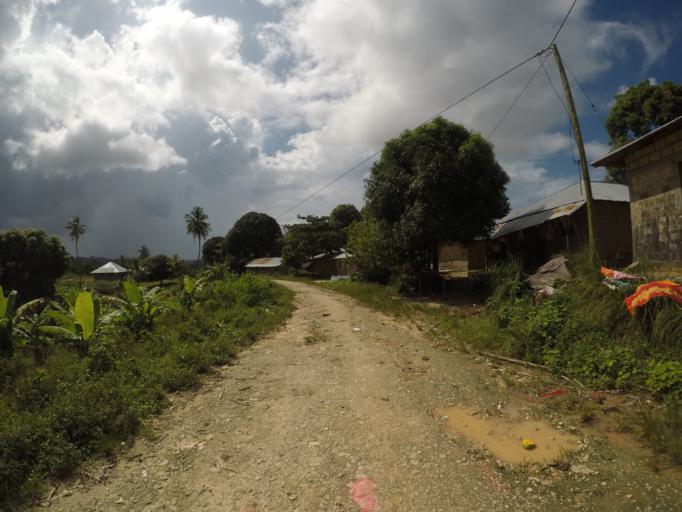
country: TZ
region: Pemba South
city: Mtambile
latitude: -5.3498
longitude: 39.7001
